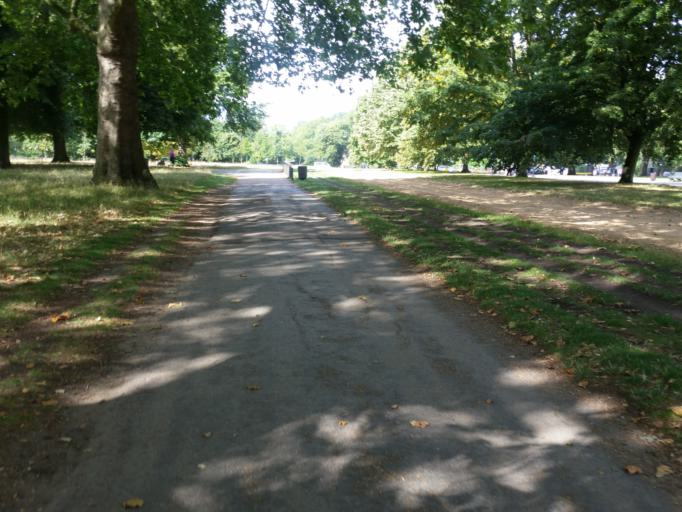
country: GB
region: England
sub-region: Greater London
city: Bayswater
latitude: 51.5115
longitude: -0.1704
